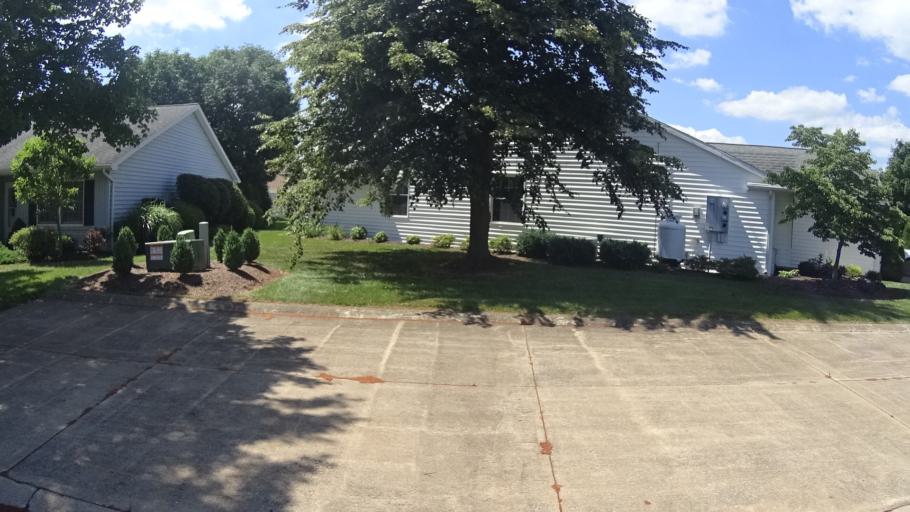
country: US
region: Ohio
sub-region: Erie County
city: Huron
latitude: 41.3845
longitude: -82.5634
